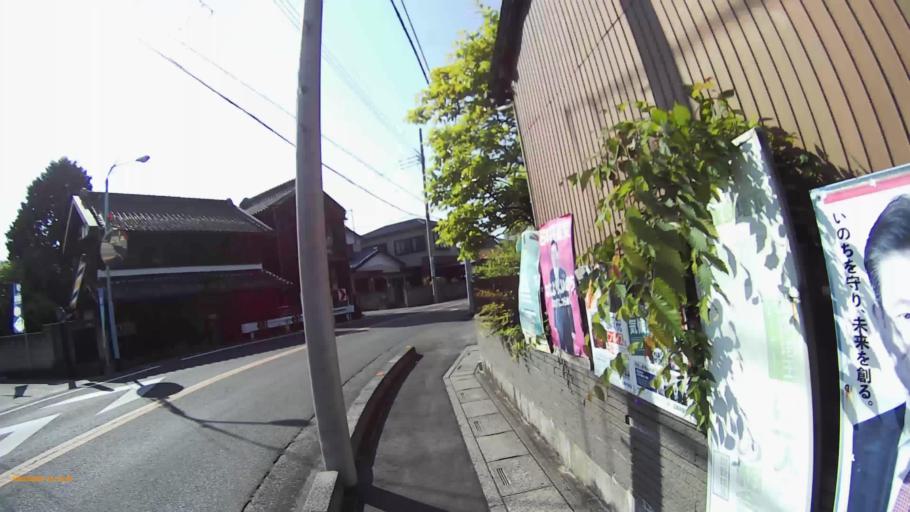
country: JP
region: Saitama
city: Sugito
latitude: 36.0310
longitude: 139.7258
